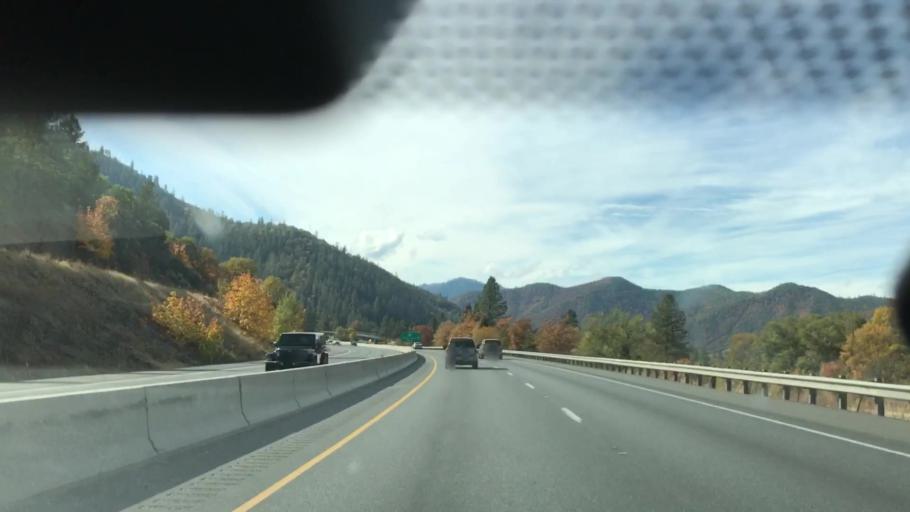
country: US
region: Oregon
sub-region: Jackson County
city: Gold Hill
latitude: 42.4313
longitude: -123.0896
